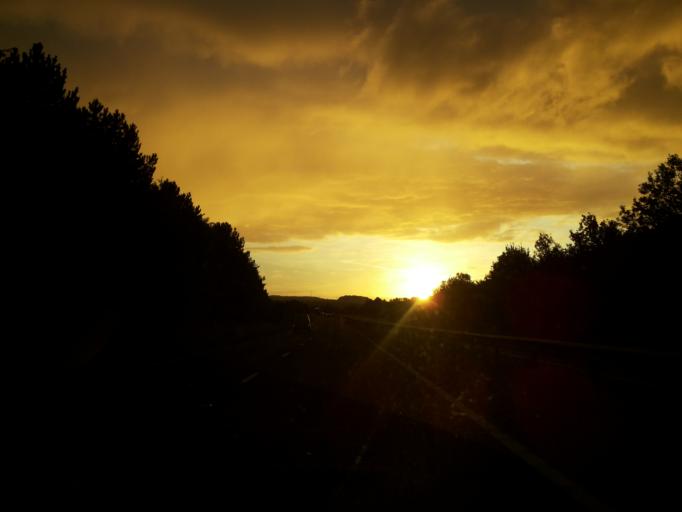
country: GB
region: England
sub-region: Wiltshire
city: Tidworth
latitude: 51.1932
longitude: -1.6623
